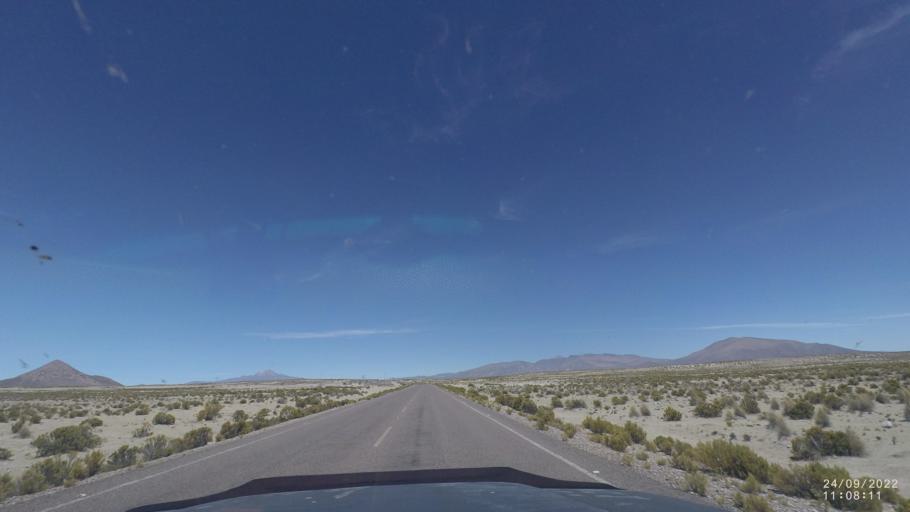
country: BO
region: Oruro
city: Challapata
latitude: -19.4827
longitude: -67.4390
